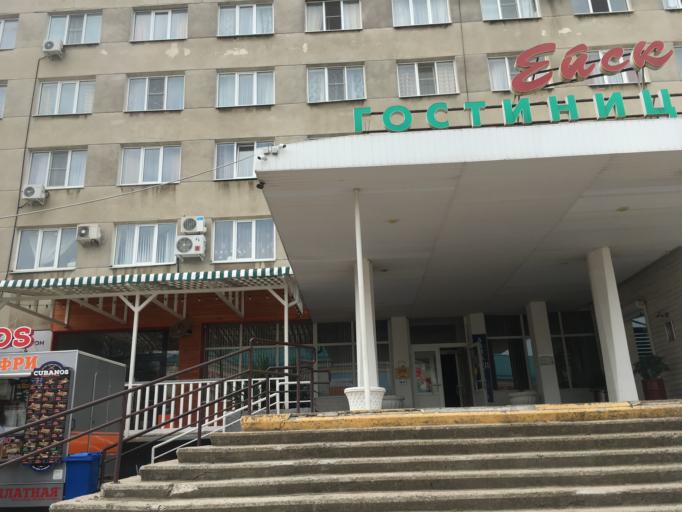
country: RU
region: Krasnodarskiy
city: Yeysk
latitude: 46.7117
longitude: 38.2757
